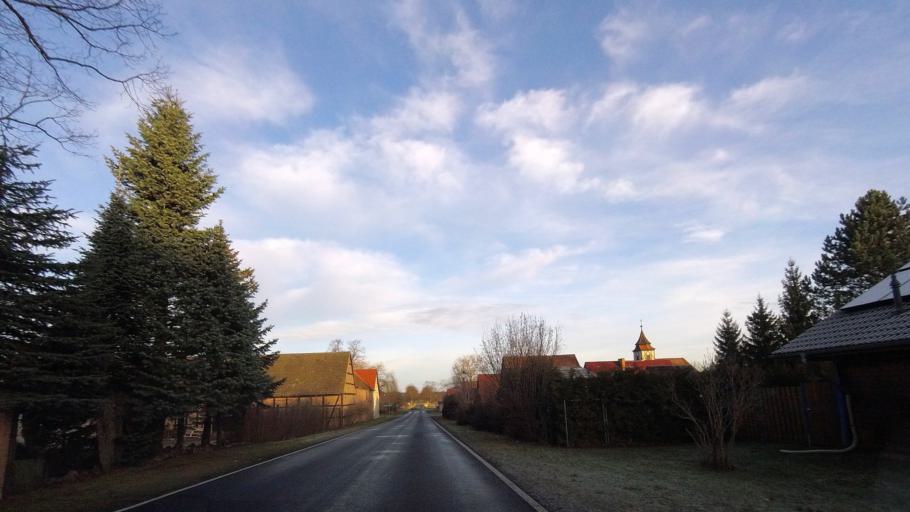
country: DE
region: Brandenburg
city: Niedergorsdorf
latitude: 52.0478
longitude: 12.9428
